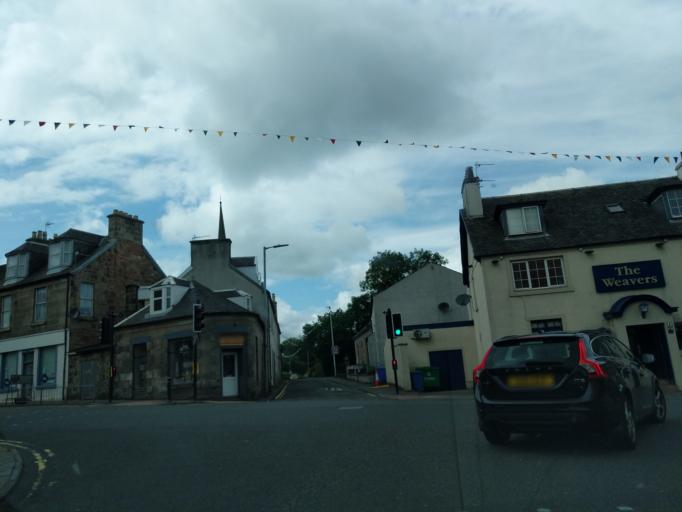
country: GB
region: Scotland
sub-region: South Lanarkshire
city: Strathaven
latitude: 55.6770
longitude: -4.0667
